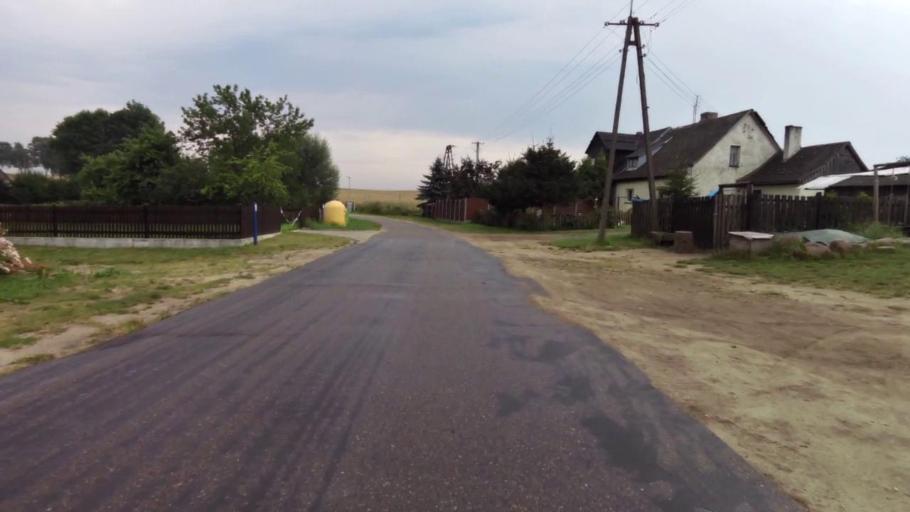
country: PL
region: West Pomeranian Voivodeship
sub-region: Powiat drawski
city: Drawsko Pomorskie
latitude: 53.5296
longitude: 15.7619
